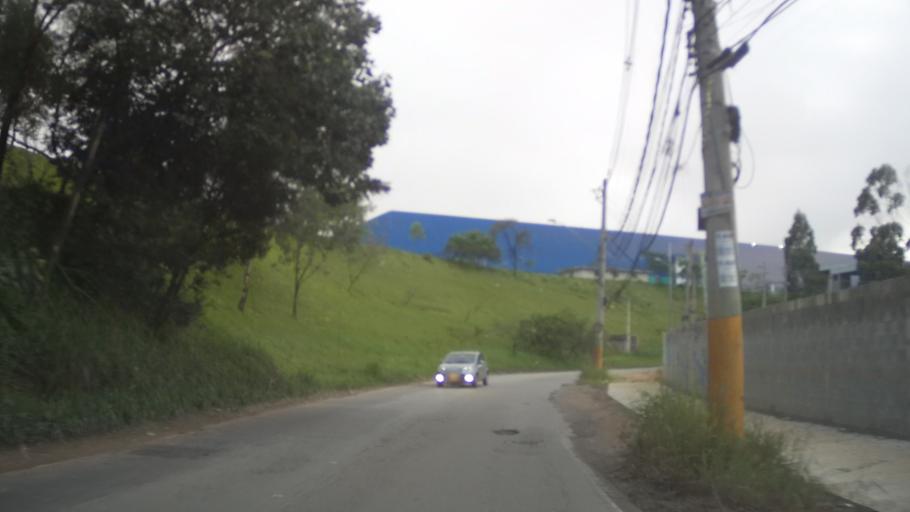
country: BR
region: Sao Paulo
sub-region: Itaquaquecetuba
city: Itaquaquecetuba
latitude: -23.4660
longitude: -46.4358
